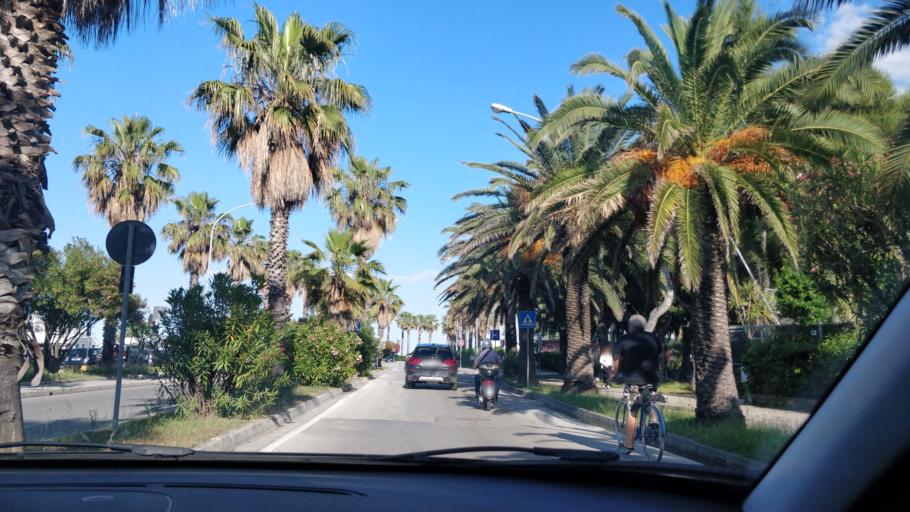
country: IT
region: The Marches
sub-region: Provincia di Ascoli Piceno
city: Grottammare
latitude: 42.9523
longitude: 13.8862
